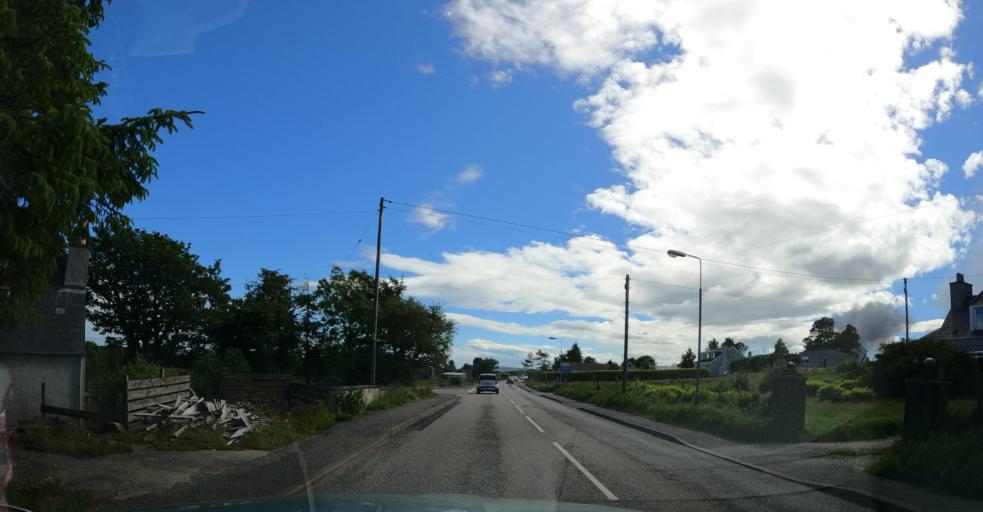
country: GB
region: Scotland
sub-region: Eilean Siar
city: Isle of Lewis
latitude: 58.2338
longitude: -6.3903
